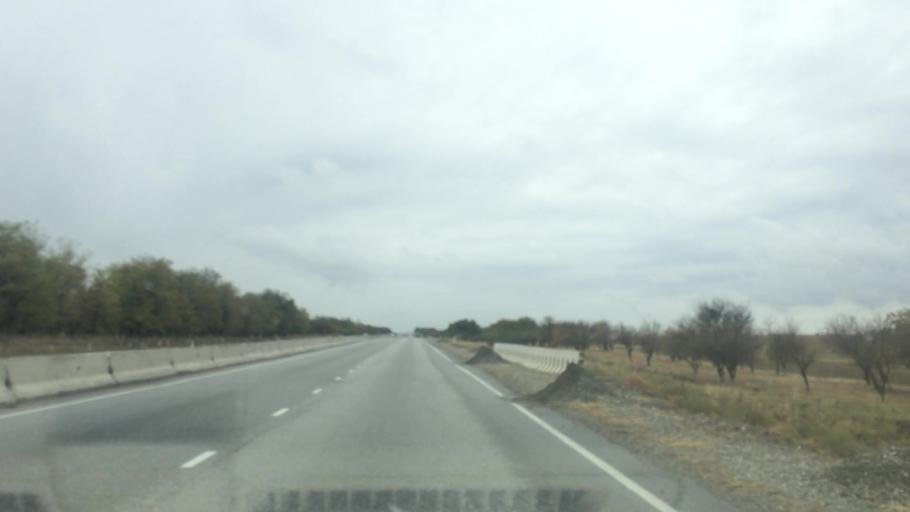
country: UZ
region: Samarqand
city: Bulung'ur
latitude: 39.8672
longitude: 67.4753
